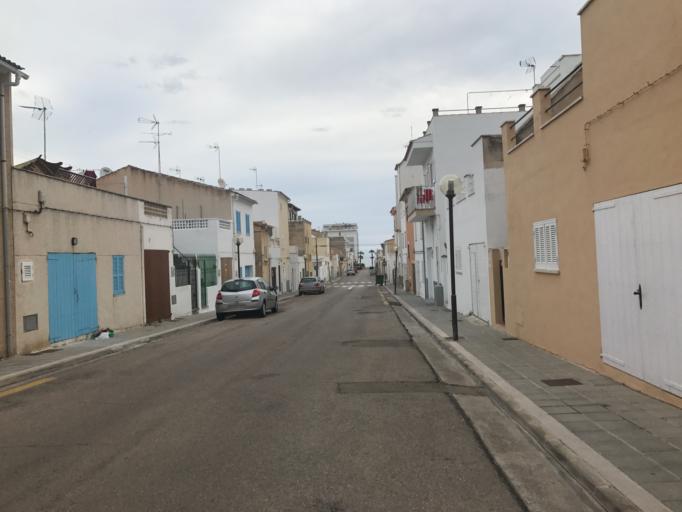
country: ES
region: Balearic Islands
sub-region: Illes Balears
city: Port d'Alcudia
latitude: 39.7639
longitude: 3.1539
